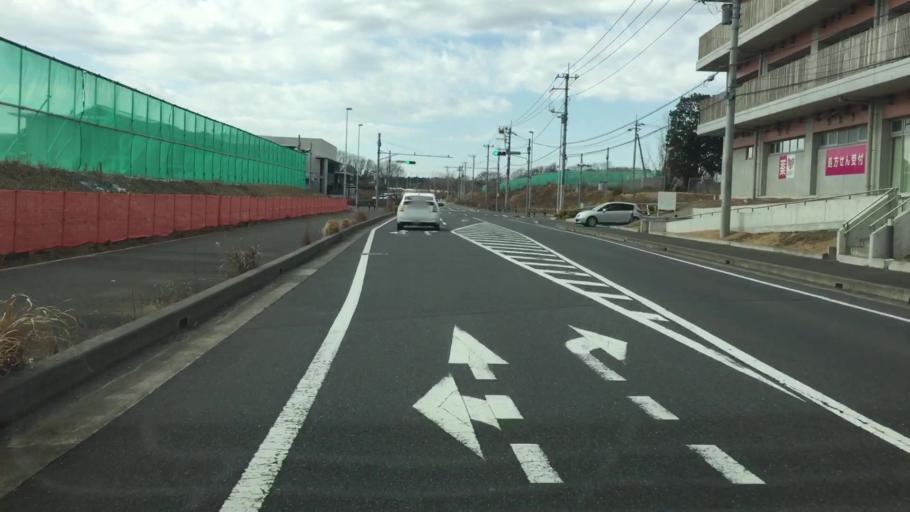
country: JP
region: Ibaraki
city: Ryugasaki
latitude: 35.8126
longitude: 140.1630
